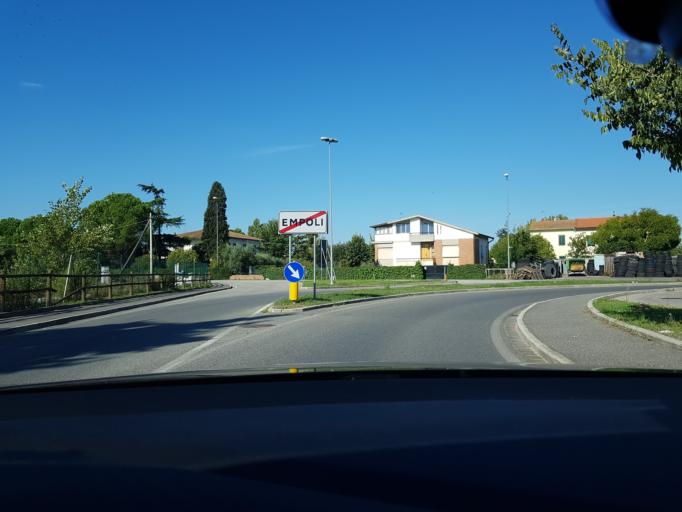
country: IT
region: Tuscany
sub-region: Province of Florence
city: Empoli
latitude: 43.7127
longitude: 10.9198
